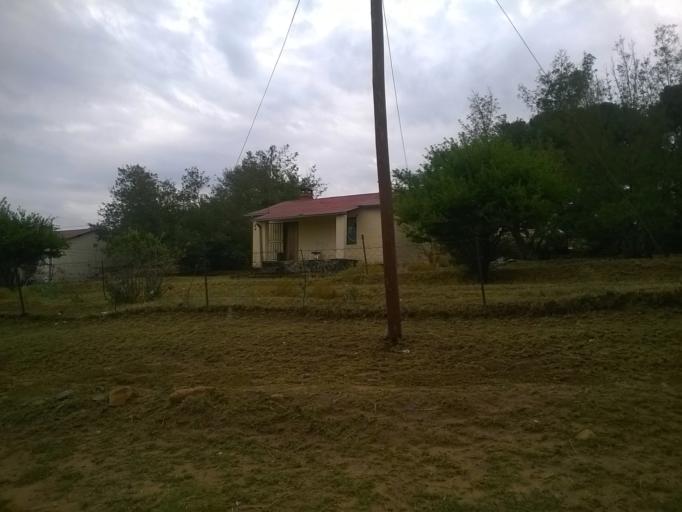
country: LS
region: Berea
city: Teyateyaneng
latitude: -29.1424
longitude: 27.7405
